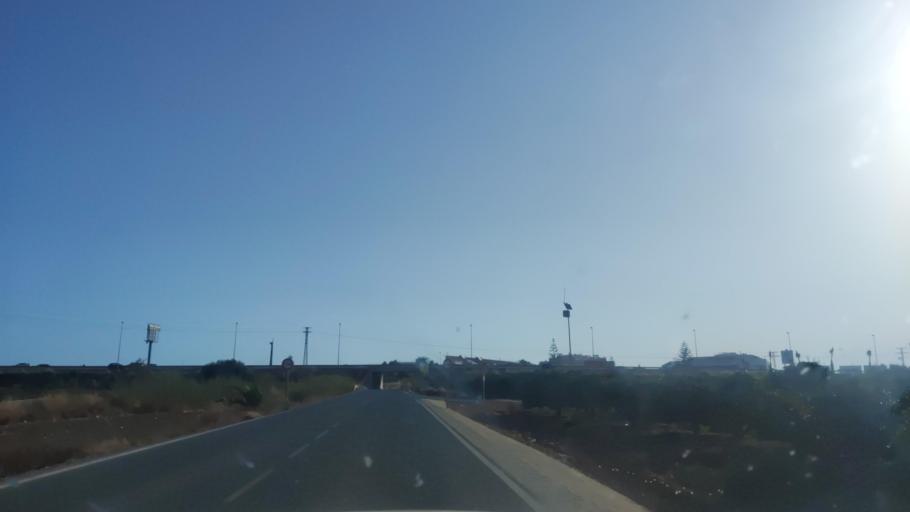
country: ES
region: Murcia
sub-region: Murcia
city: San Javier
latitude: 37.8047
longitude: -0.8599
